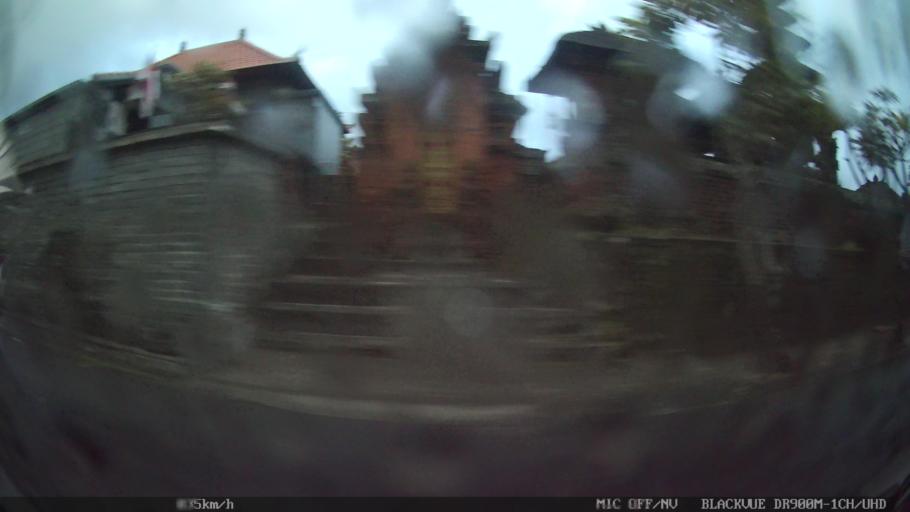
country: ID
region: Bali
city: Banjar Batur
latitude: -8.6043
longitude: 115.2209
